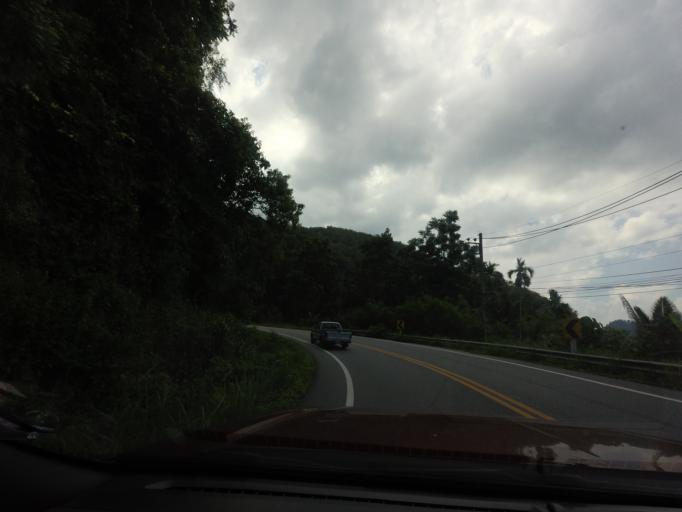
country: TH
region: Yala
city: Than To
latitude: 6.0364
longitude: 101.1966
